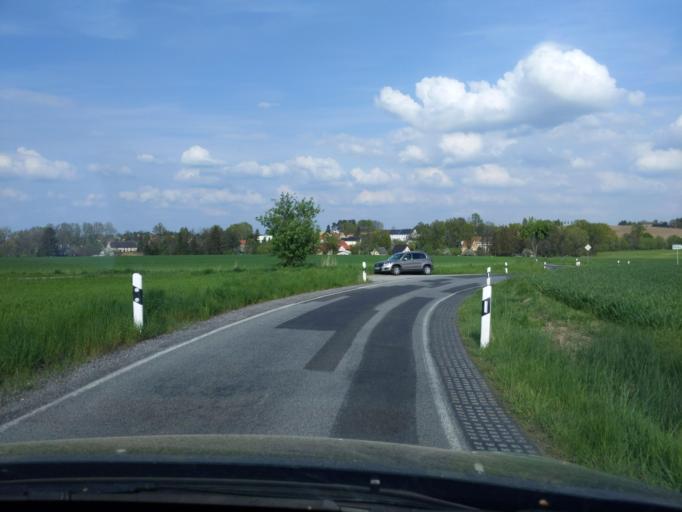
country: DE
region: Saxony
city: Kubschutz
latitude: 51.1671
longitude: 14.4796
